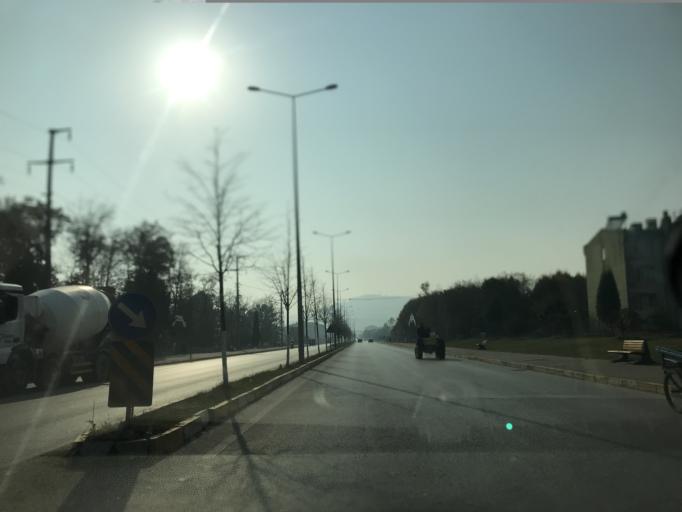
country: TR
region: Duzce
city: Cumayeri
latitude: 40.8649
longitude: 30.9528
